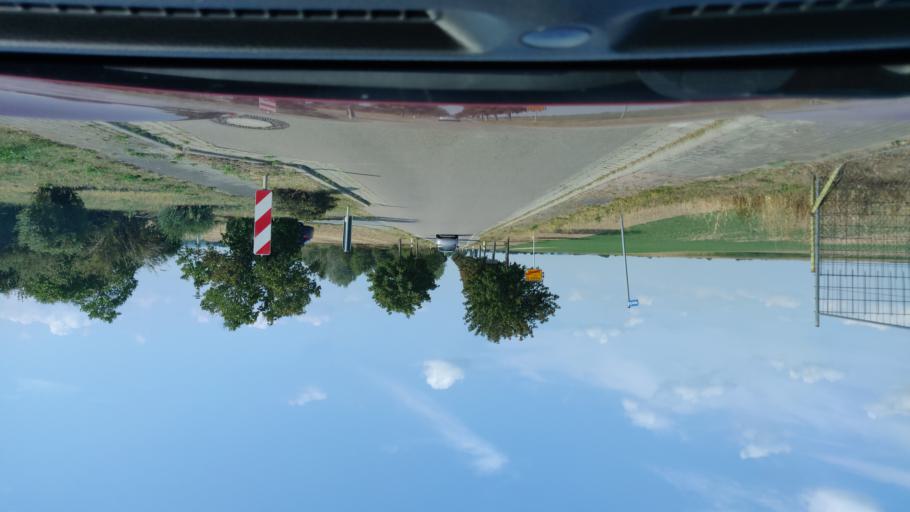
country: DE
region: Saxony
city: Mockrehna
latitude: 51.4920
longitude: 12.8342
